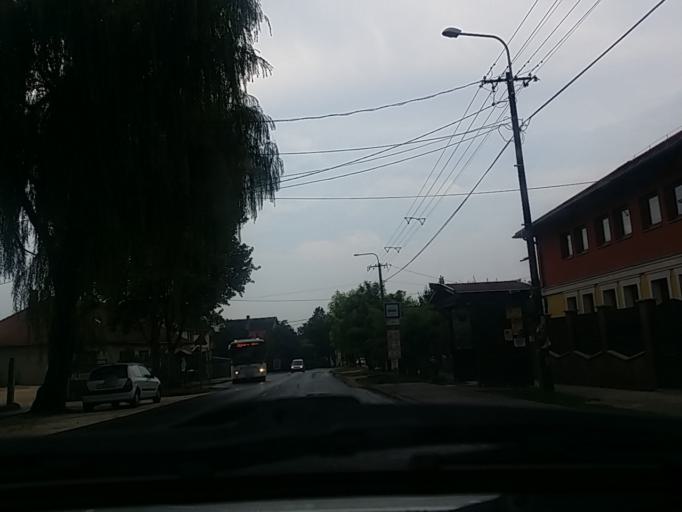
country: HU
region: Pest
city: Paty
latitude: 47.5141
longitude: 18.8268
